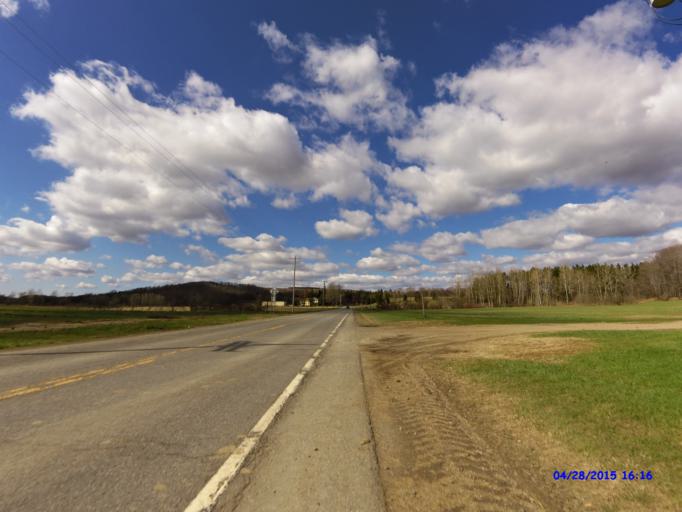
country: US
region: New York
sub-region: Cattaraugus County
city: Franklinville
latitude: 42.3681
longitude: -78.4510
